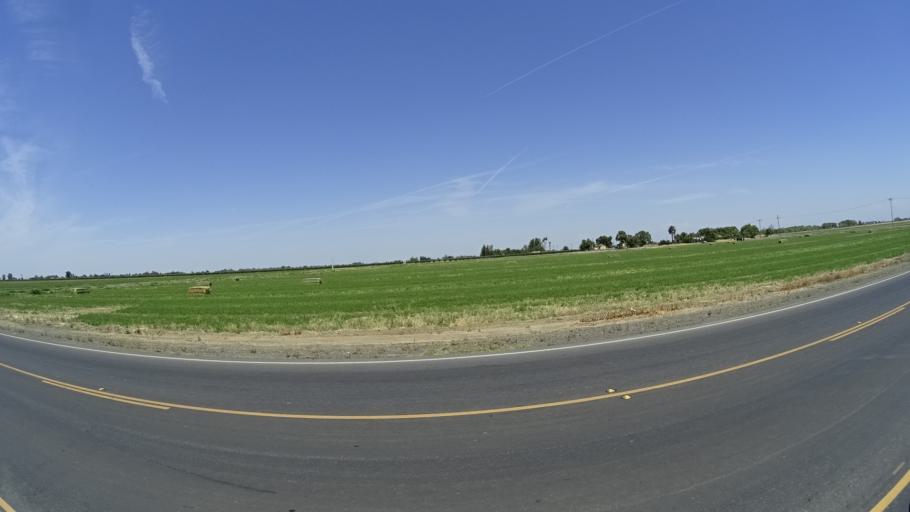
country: US
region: California
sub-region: Kings County
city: Lemoore
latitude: 36.2400
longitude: -119.7646
